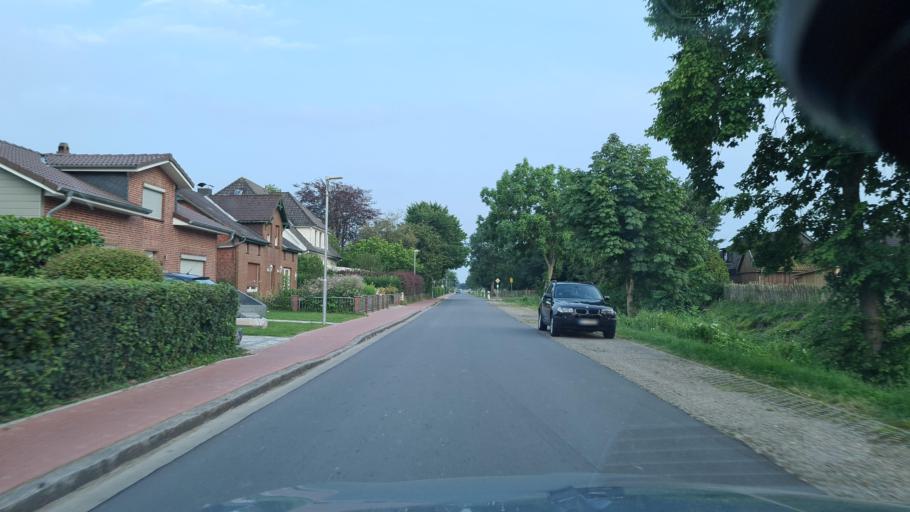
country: DE
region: Schleswig-Holstein
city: Oldenswort
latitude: 54.3712
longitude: 8.9436
